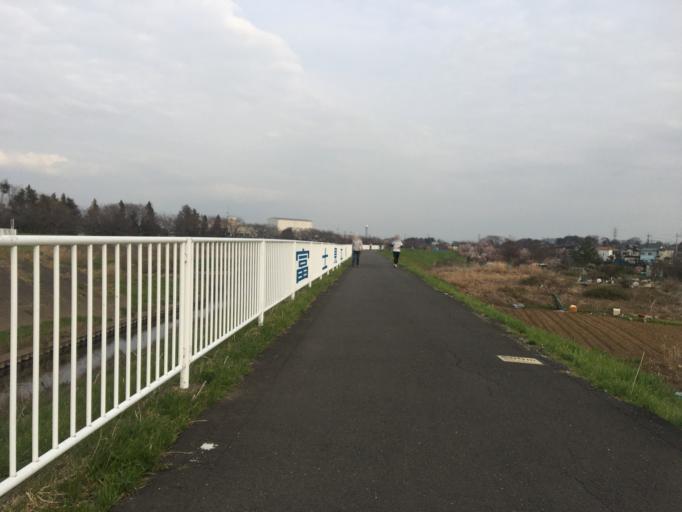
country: JP
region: Saitama
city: Shiki
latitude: 35.8506
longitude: 139.5598
